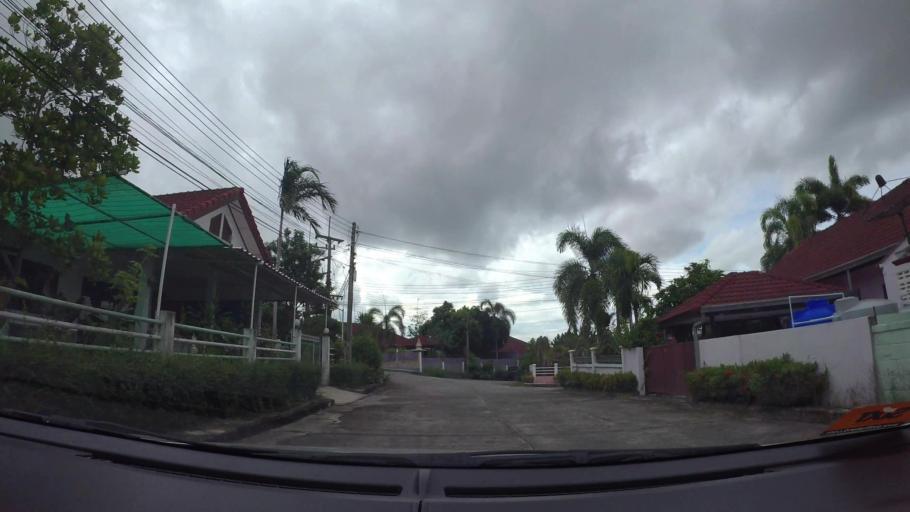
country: TH
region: Chon Buri
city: Sattahip
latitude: 12.7248
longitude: 100.9050
